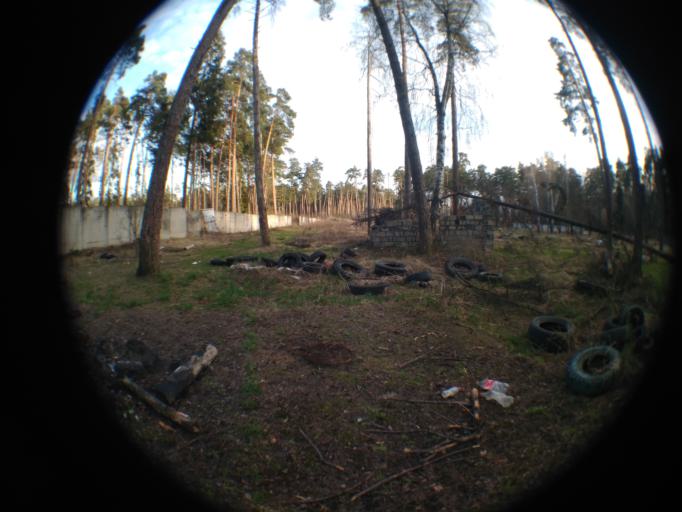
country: RU
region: Moskovskaya
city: Zhukovskiy
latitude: 55.5795
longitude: 38.1183
